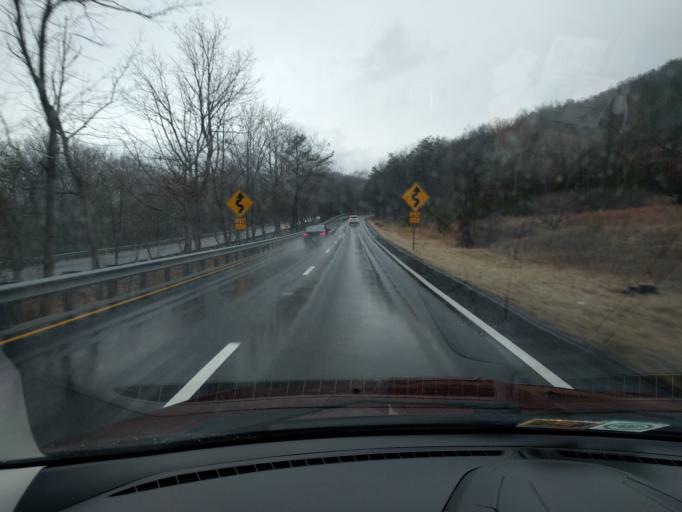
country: US
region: Virginia
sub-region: Montgomery County
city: Blacksburg
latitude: 37.2860
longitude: -80.4678
